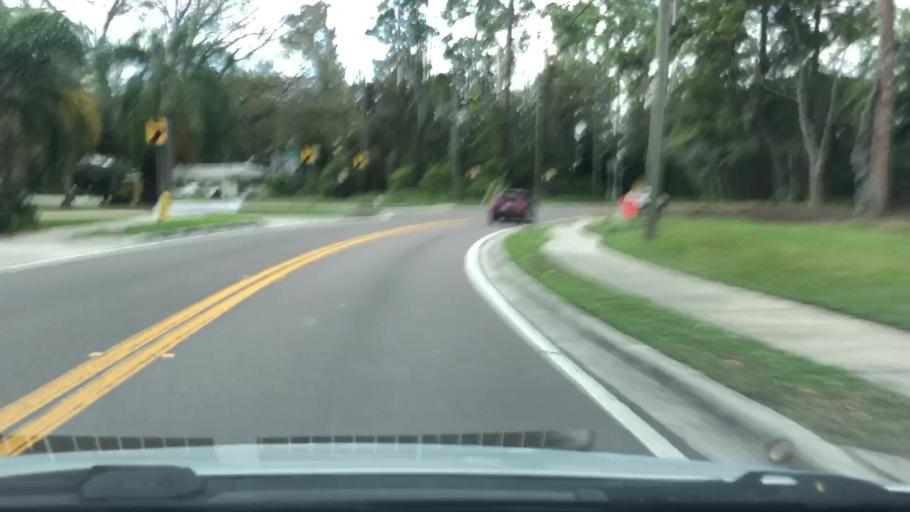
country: US
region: Florida
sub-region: Seminole County
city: Forest City
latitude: 28.6472
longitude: -81.4434
